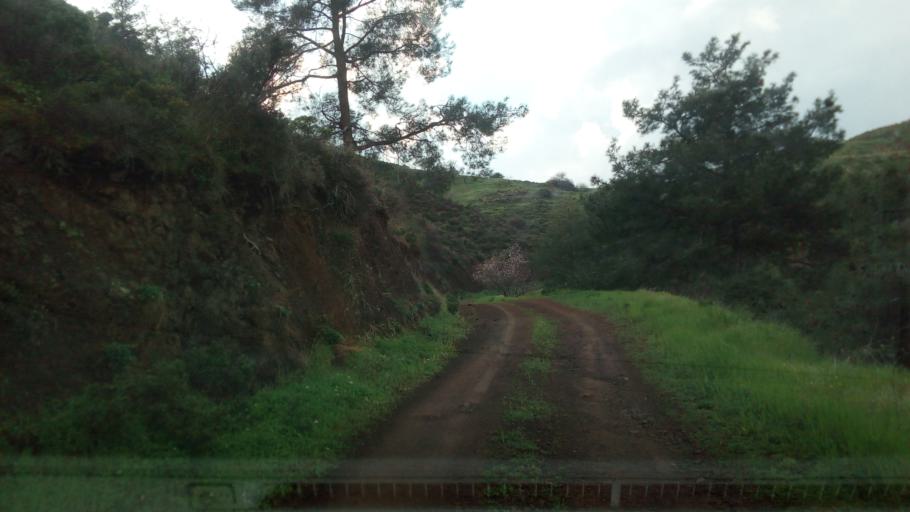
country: CY
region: Lefkosia
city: Kato Pyrgos
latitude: 35.1683
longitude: 32.6670
